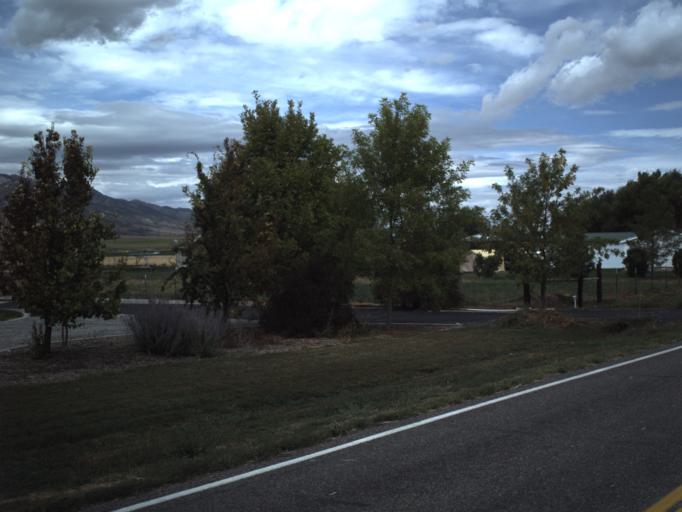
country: US
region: Utah
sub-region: Cache County
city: Benson
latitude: 41.8579
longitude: -111.9999
